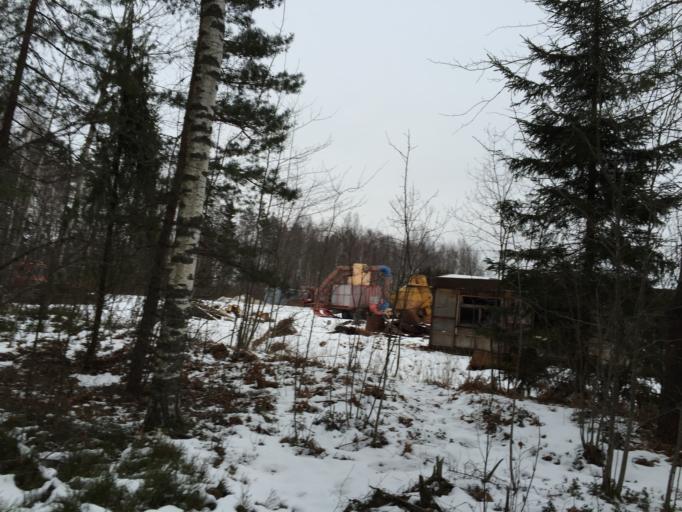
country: LV
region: Saulkrastu
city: Saulkrasti
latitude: 57.2389
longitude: 24.5057
